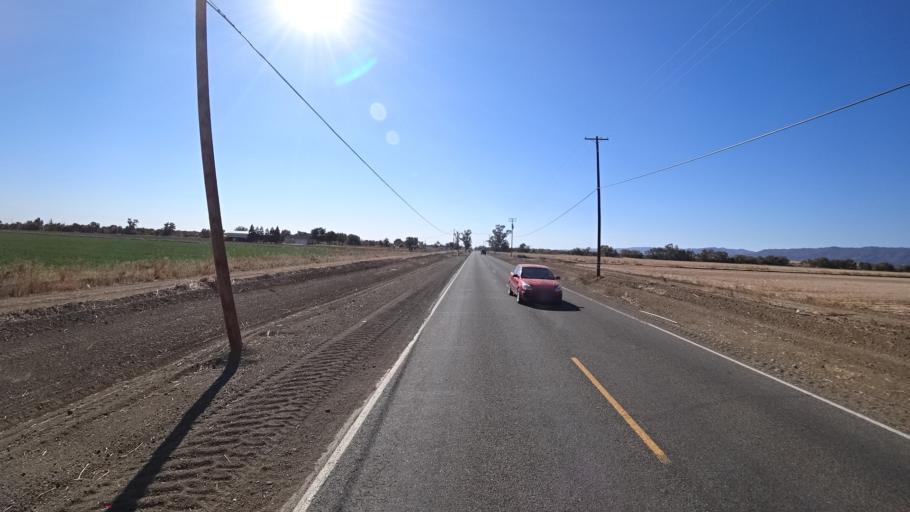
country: US
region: California
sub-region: Yolo County
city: Cottonwood
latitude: 38.6107
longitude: -121.9714
